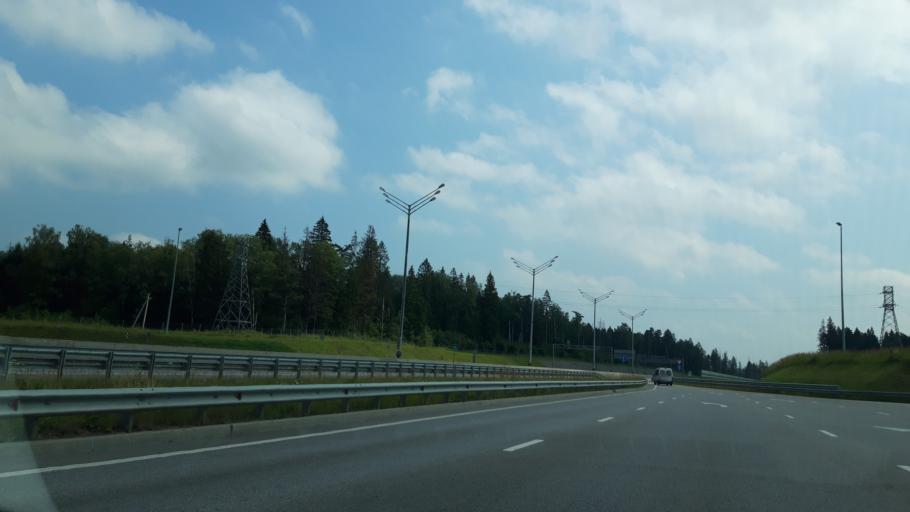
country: RU
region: Moskovskaya
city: Radumlya
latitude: 56.0961
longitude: 37.1850
